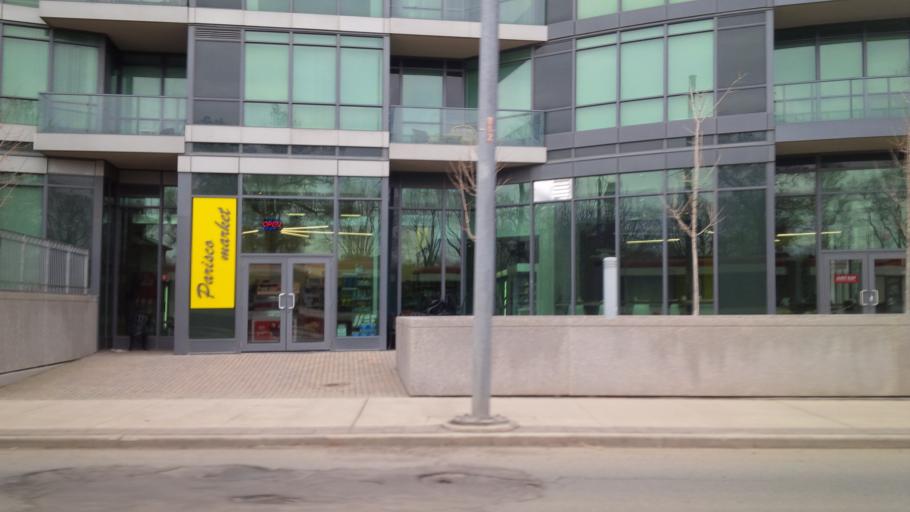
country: CA
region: Ontario
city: Toronto
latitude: 43.6360
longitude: -79.4048
